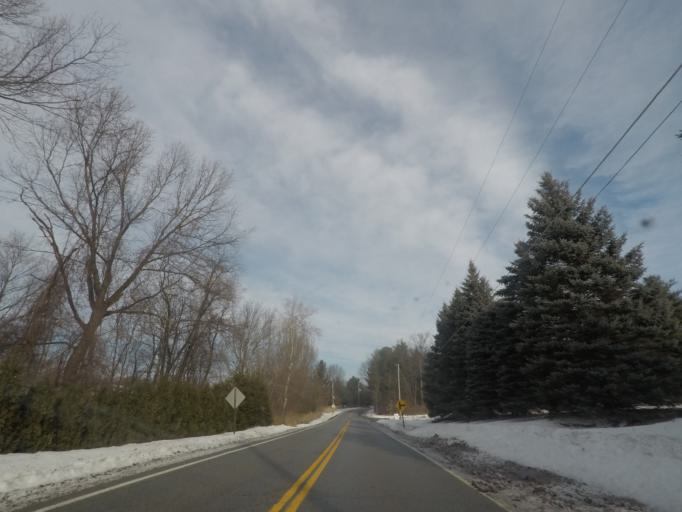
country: US
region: New York
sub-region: Saratoga County
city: Country Knolls
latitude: 42.8758
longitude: -73.7513
